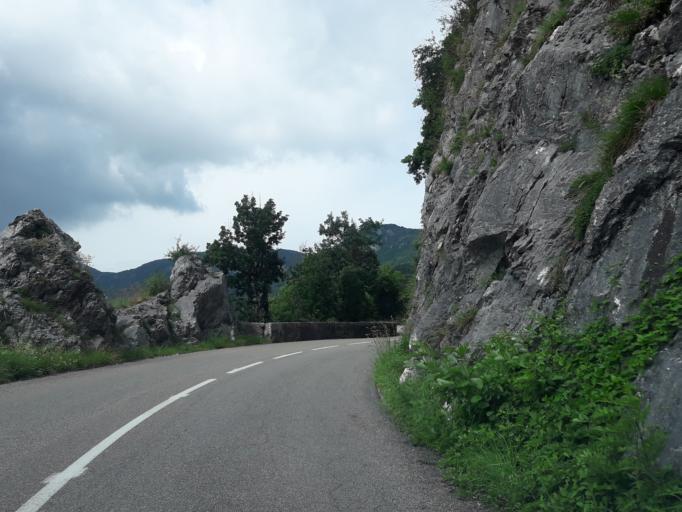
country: FR
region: Rhone-Alpes
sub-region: Departement de la Savoie
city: Le Bourget-du-Lac
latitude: 45.6919
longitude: 5.8360
